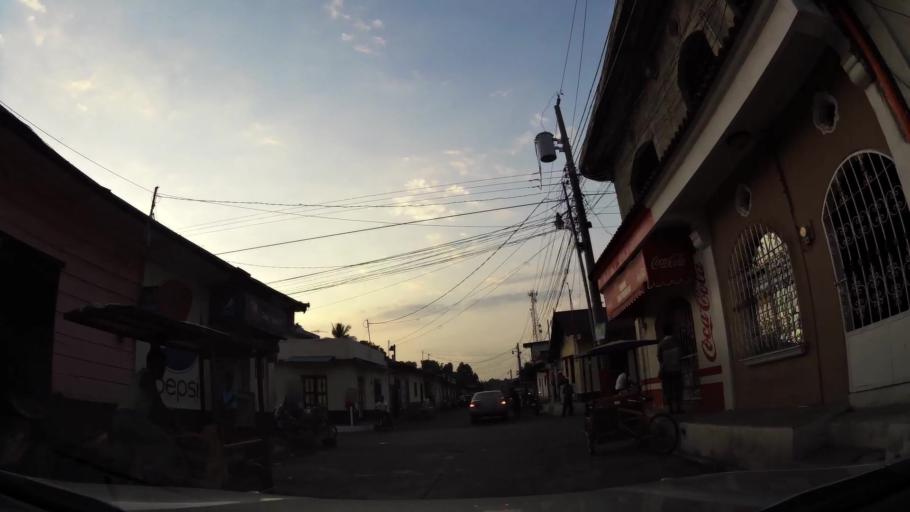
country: GT
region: Retalhuleu
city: San Sebastian
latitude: 14.5638
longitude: -91.6497
